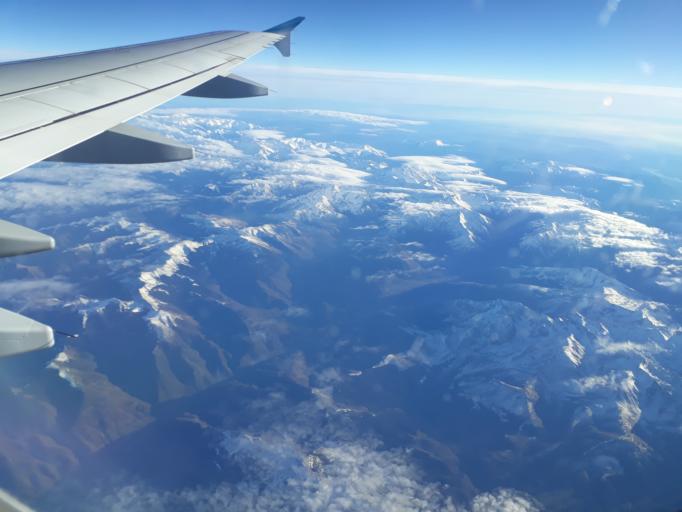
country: FR
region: Midi-Pyrenees
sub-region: Departement des Hautes-Pyrenees
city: Gerde
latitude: 43.0607
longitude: 0.2455
